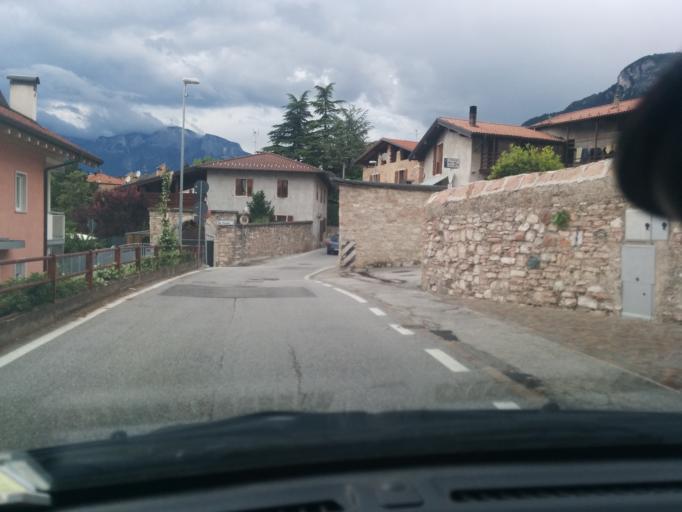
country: IT
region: Trentino-Alto Adige
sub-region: Provincia di Trento
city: Povo
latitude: 46.0735
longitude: 11.1474
